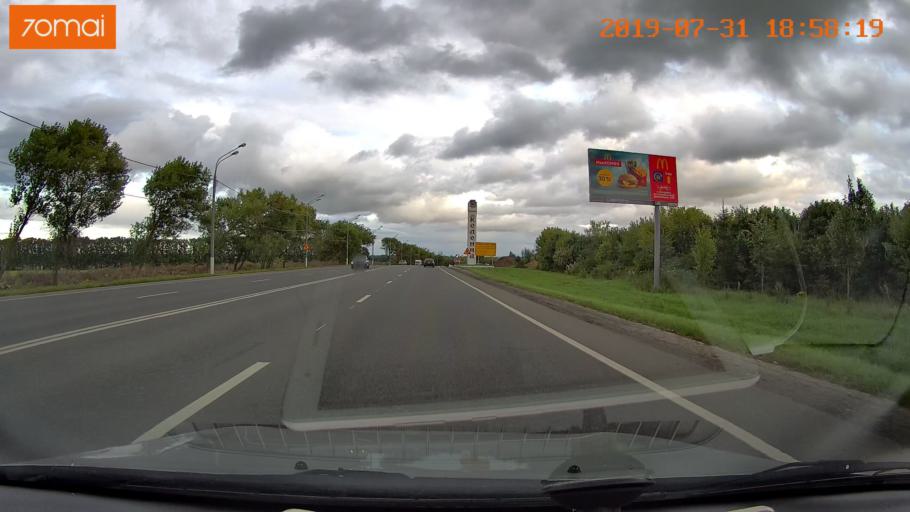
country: RU
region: Moskovskaya
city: Raduzhnyy
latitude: 55.1477
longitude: 38.7032
